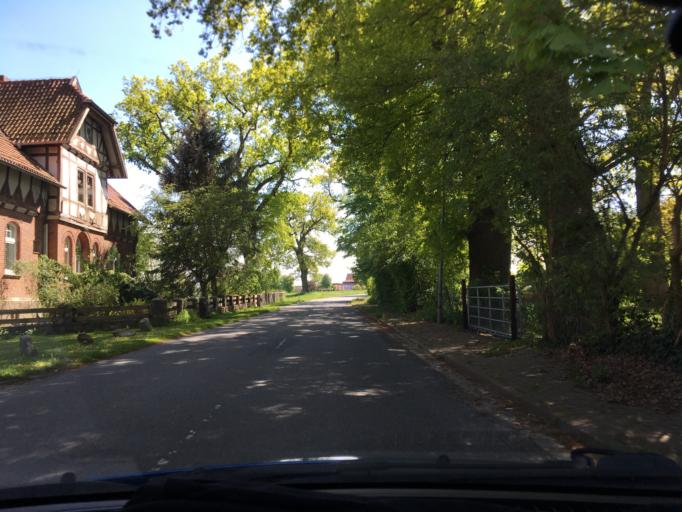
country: DE
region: Lower Saxony
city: Waddeweitz
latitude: 53.0076
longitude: 10.9039
